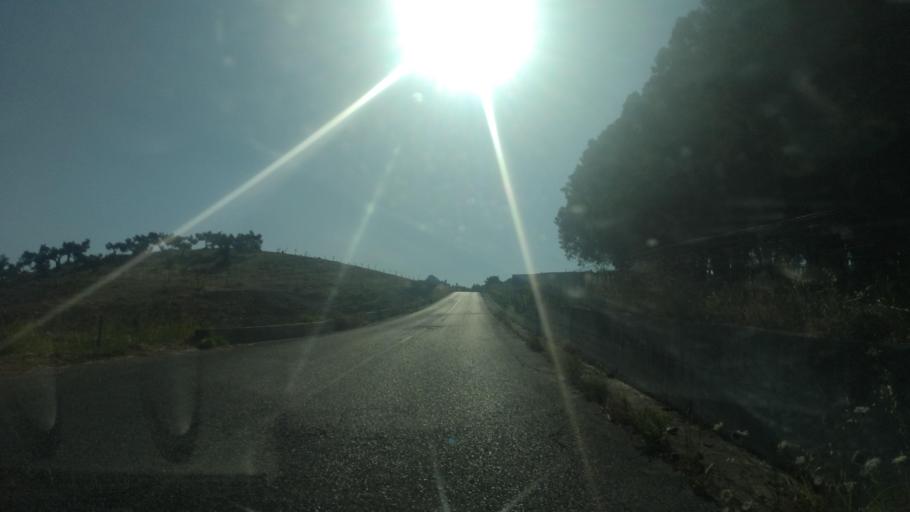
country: IT
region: Calabria
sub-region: Provincia di Catanzaro
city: Squillace
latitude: 38.7786
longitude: 16.5028
